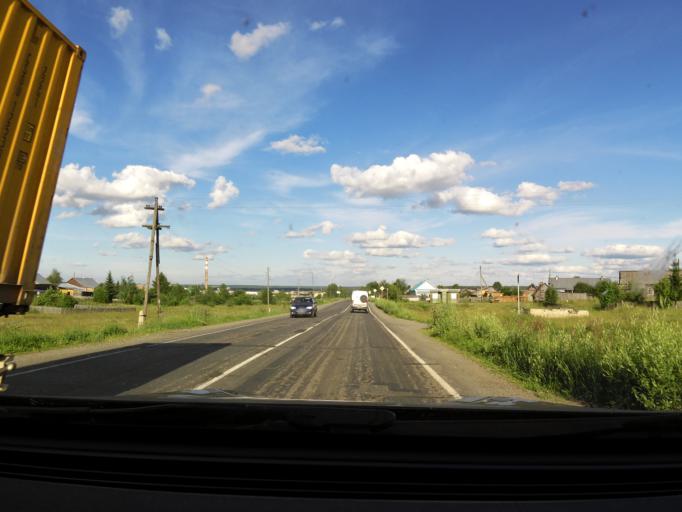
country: RU
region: Kirov
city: Omutninsk
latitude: 58.6928
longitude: 52.2050
